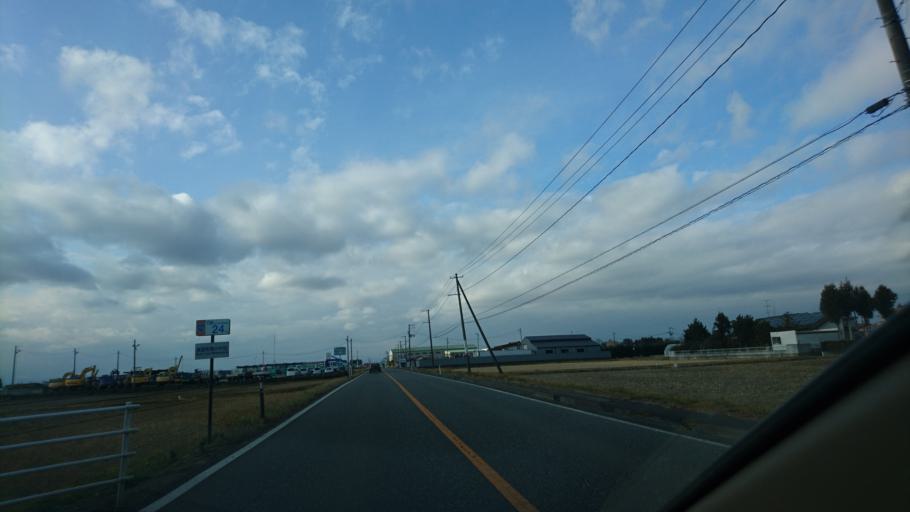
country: JP
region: Miyagi
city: Kogota
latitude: 38.5524
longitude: 141.0905
